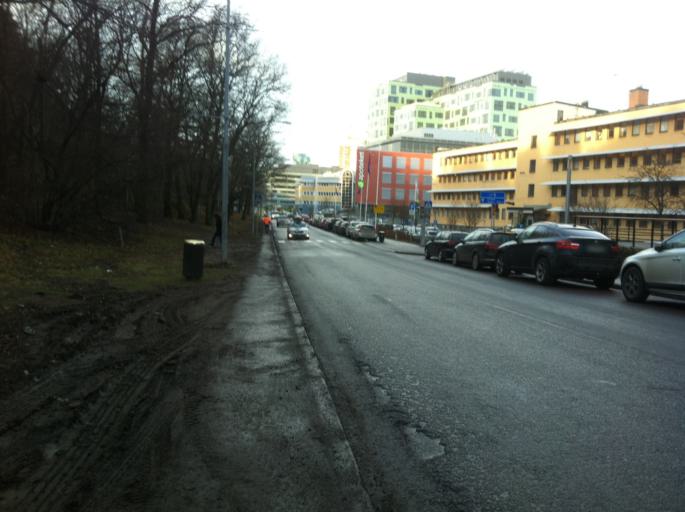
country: SE
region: Stockholm
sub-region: Solna Kommun
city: Solna
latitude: 59.3667
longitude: 18.0060
